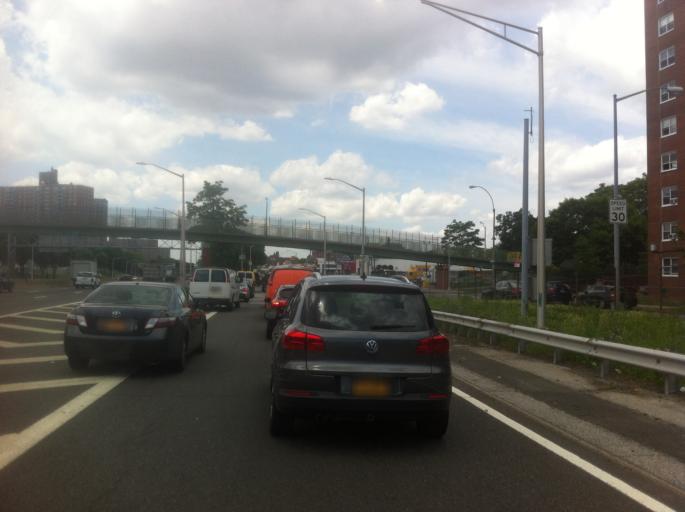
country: US
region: New York
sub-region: Bronx
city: The Bronx
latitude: 40.8267
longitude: -73.8554
